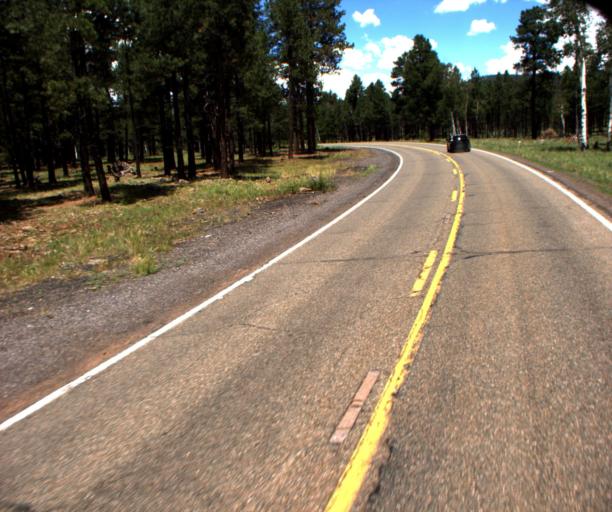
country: US
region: Arizona
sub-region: Coconino County
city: Flagstaff
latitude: 35.3237
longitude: -111.7730
